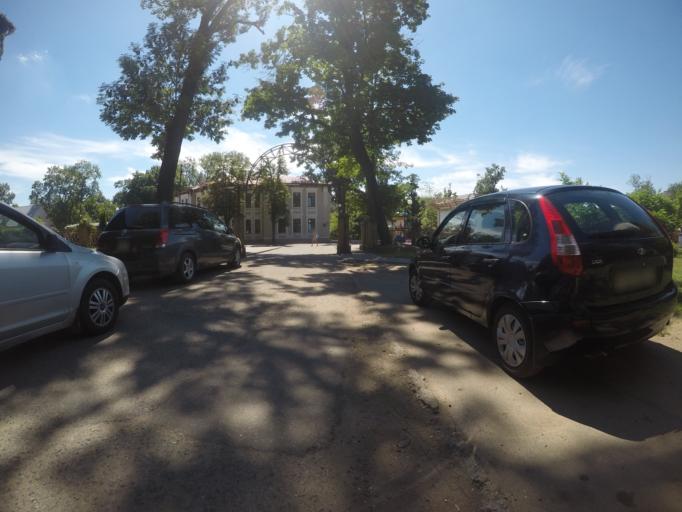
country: BY
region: Grodnenskaya
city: Hrodna
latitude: 53.6844
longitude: 23.8383
